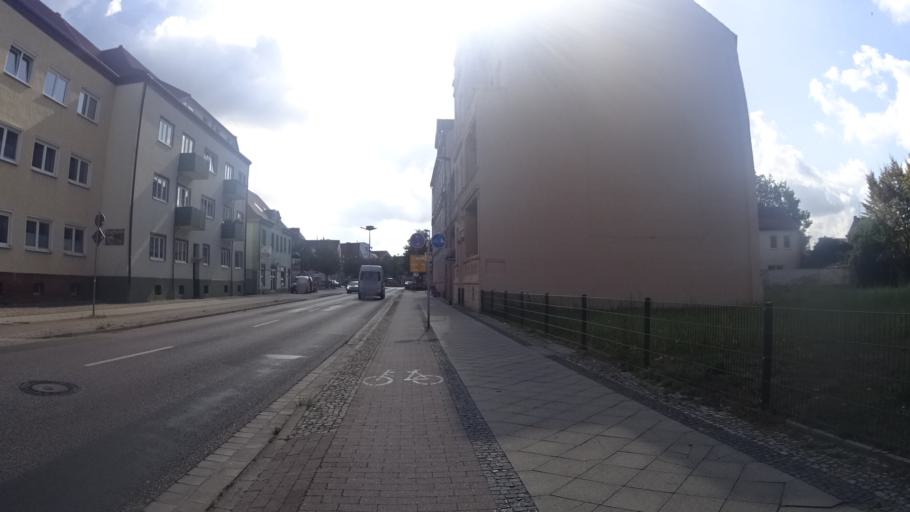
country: DE
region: Brandenburg
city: Wittenberge
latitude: 52.9954
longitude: 11.7506
